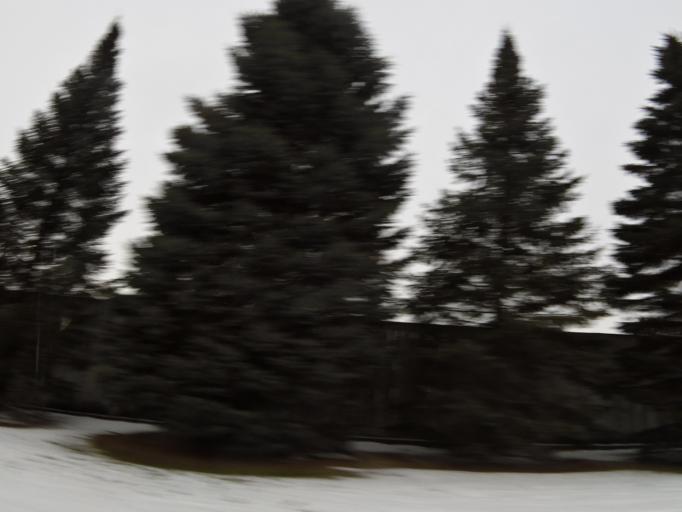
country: US
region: Minnesota
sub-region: Washington County
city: Stillwater
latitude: 45.0320
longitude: -92.8386
